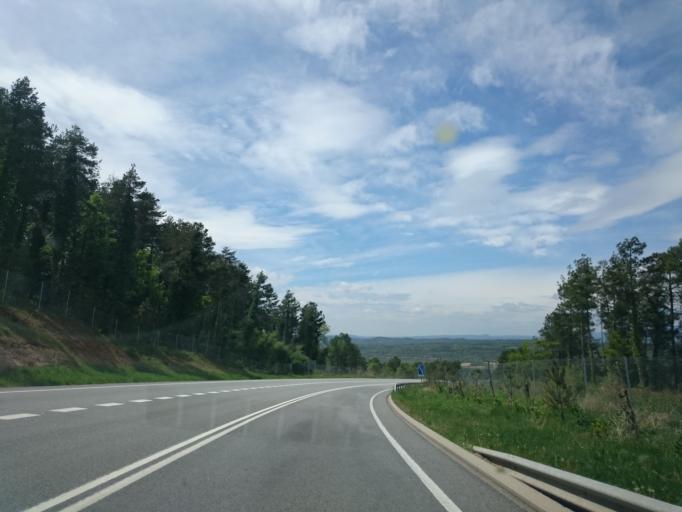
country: ES
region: Catalonia
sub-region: Provincia de Barcelona
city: Prats de Llucanes
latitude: 42.0188
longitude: 2.0129
